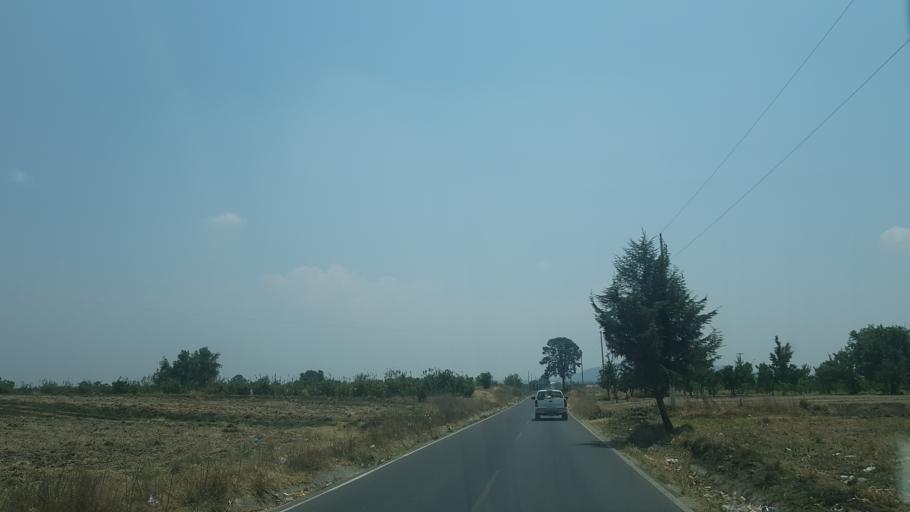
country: MX
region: Puebla
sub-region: San Jeronimo Tecuanipan
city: San Miguel Papaxtla
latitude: 19.0958
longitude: -98.4097
